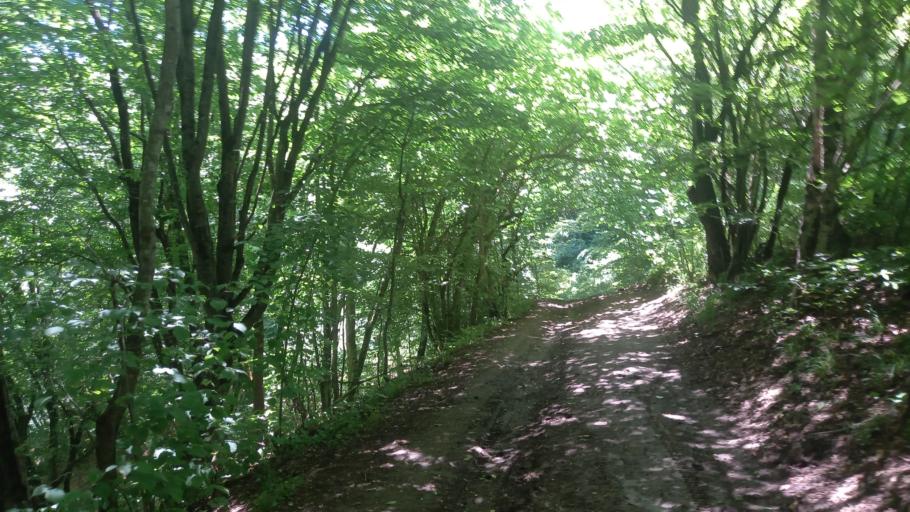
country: RU
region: Karachayevo-Cherkesiya
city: Pregradnaya
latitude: 44.1040
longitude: 41.1381
